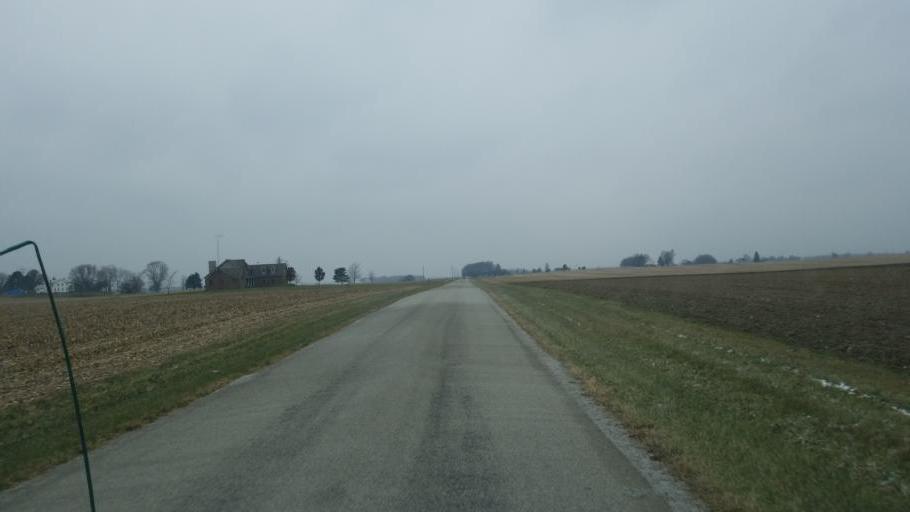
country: US
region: Ohio
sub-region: Richland County
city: Shelby
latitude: 40.8852
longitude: -82.7151
